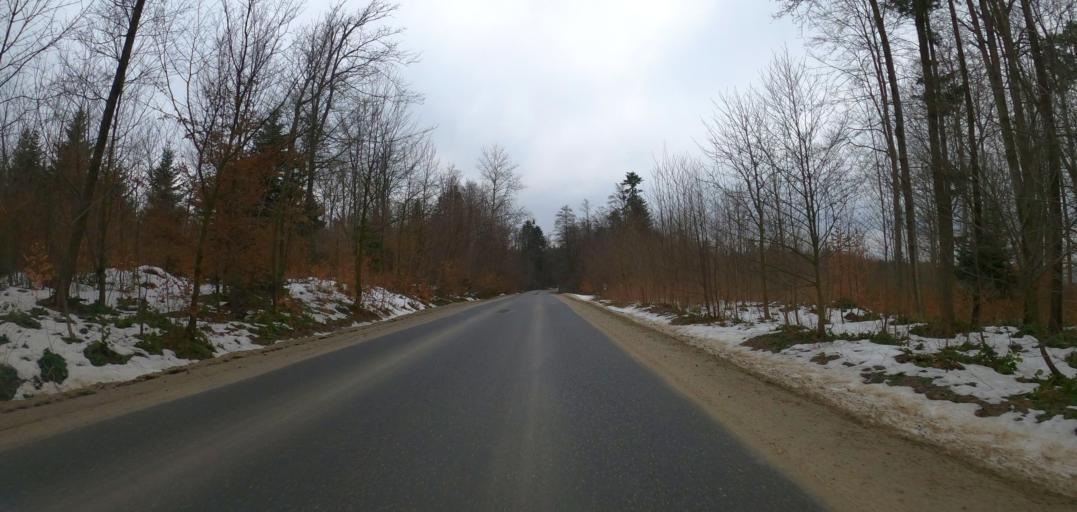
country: PL
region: Subcarpathian Voivodeship
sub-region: Powiat debicki
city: Debica
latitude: 49.9800
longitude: 21.4089
